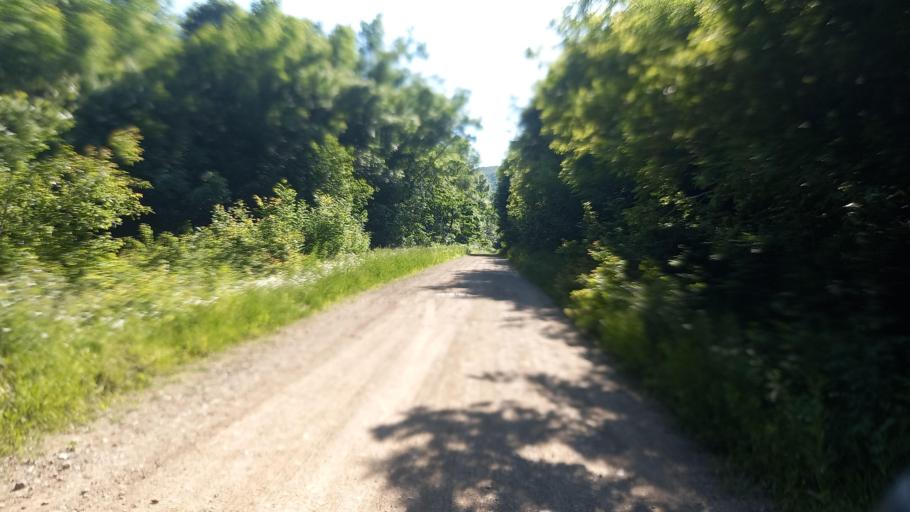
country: RU
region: Krasnodarskiy
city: Dzhubga
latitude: 44.5376
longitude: 38.7760
